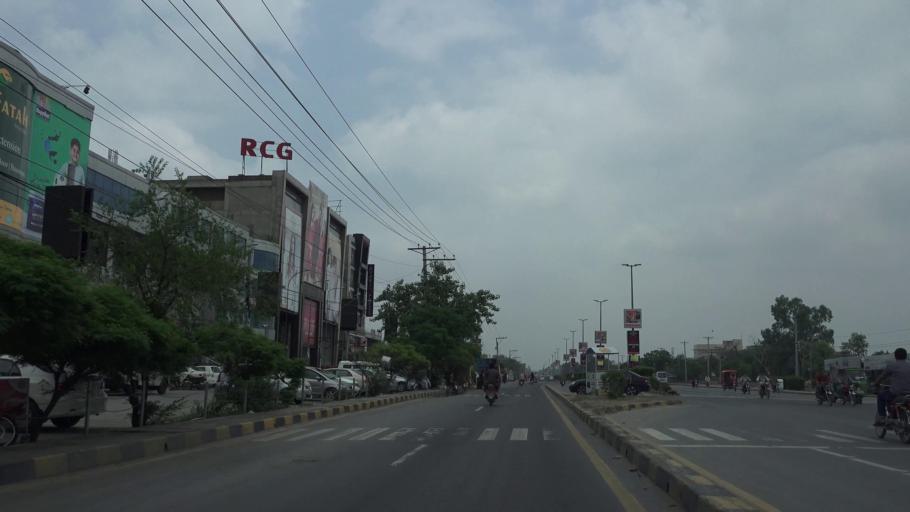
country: PK
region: Punjab
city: Faisalabad
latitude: 31.4057
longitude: 73.1235
